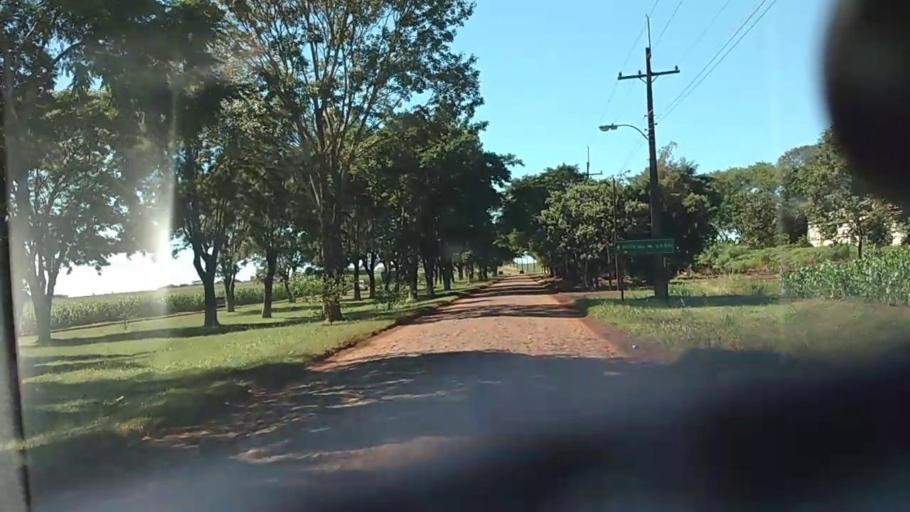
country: PY
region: Alto Parana
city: Naranjal
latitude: -25.9764
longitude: -55.1767
